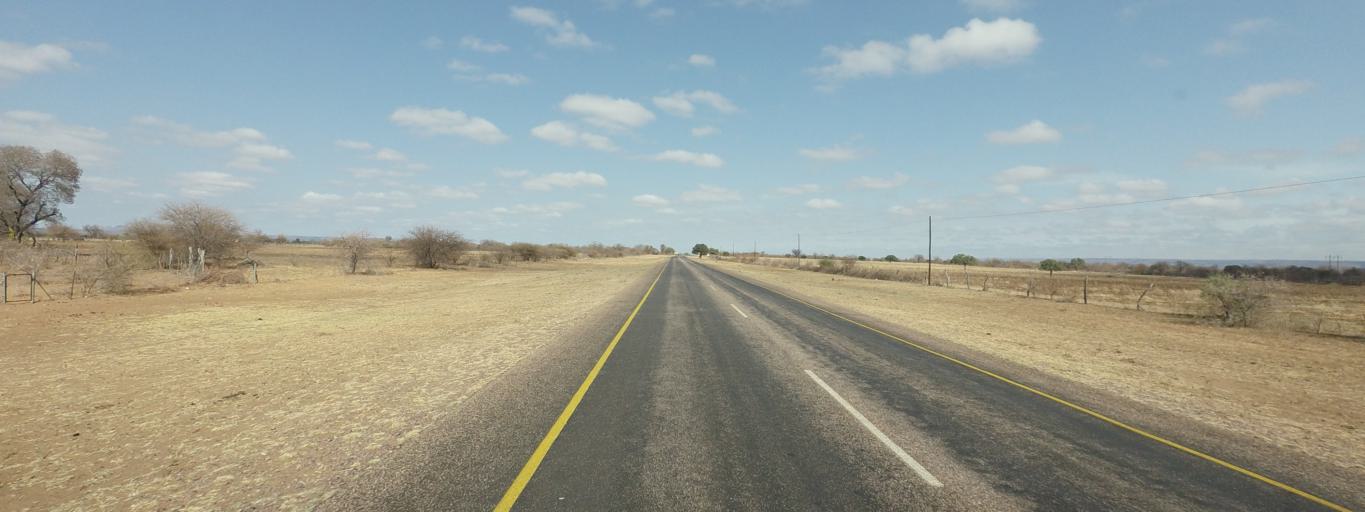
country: BW
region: Central
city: Ramokgonami
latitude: -22.8022
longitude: 27.5016
